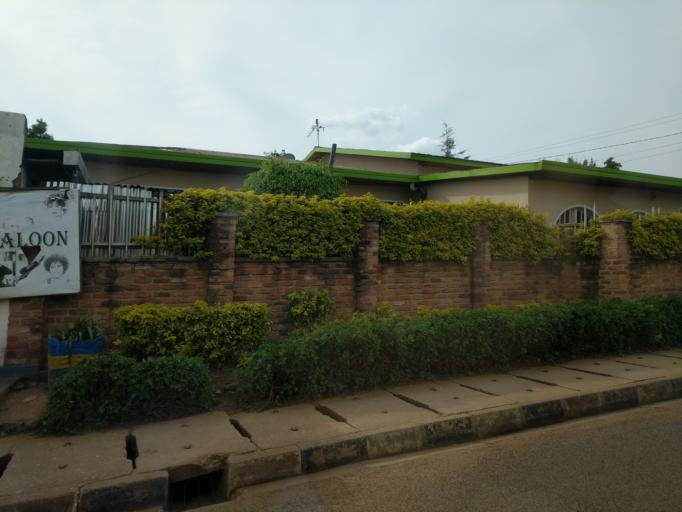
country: RW
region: Kigali
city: Kigali
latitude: -1.9816
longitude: 30.1330
